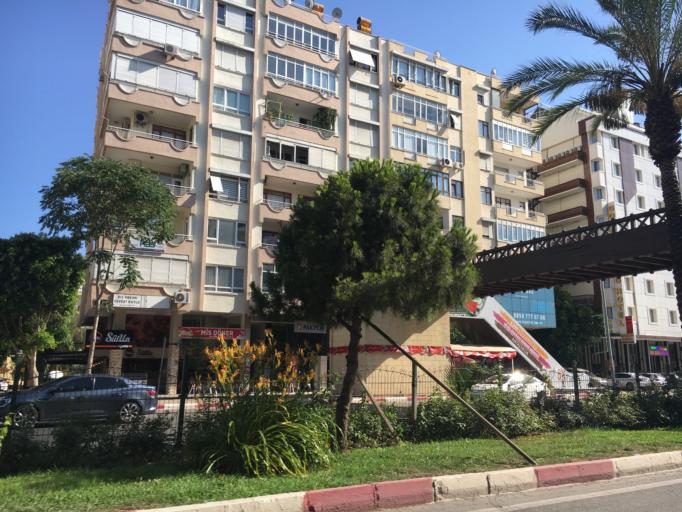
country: TR
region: Antalya
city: Antalya
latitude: 36.8885
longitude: 30.6810
